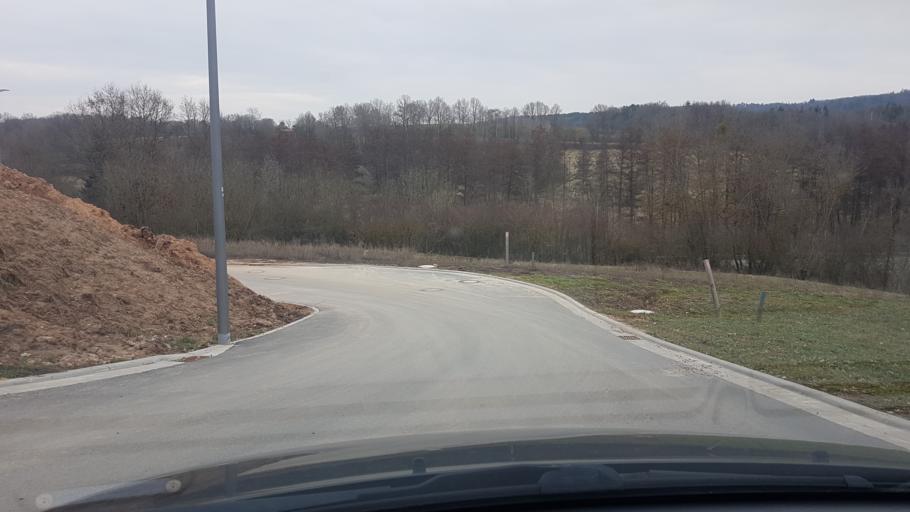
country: DE
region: Bavaria
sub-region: Upper Franconia
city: Baunach
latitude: 49.9833
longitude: 10.8369
